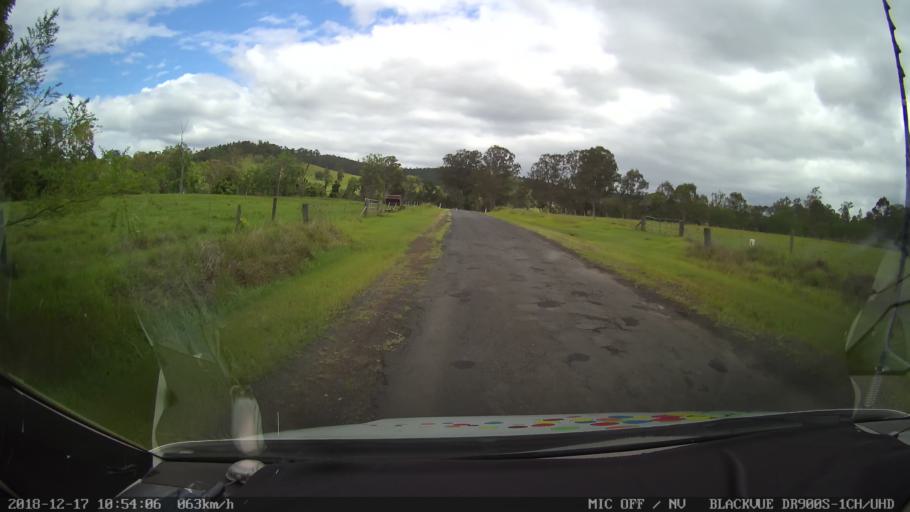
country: AU
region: New South Wales
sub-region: Tenterfield Municipality
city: Carrolls Creek
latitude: -28.8316
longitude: 152.5654
